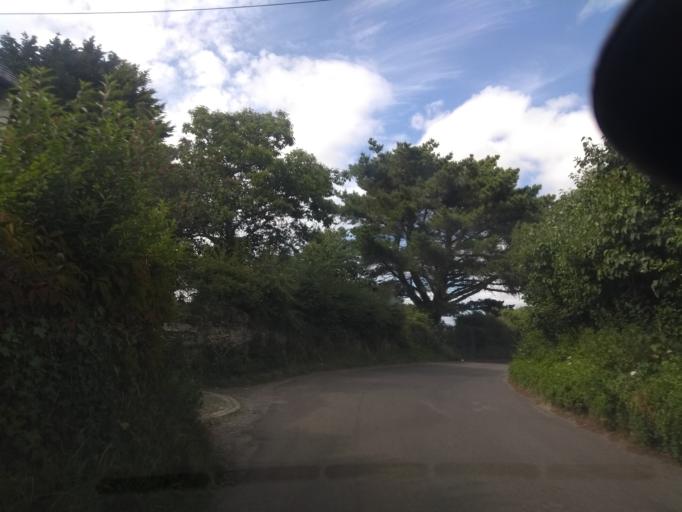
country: GB
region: England
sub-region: Devon
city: Modbury
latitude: 50.3060
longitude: -3.8854
